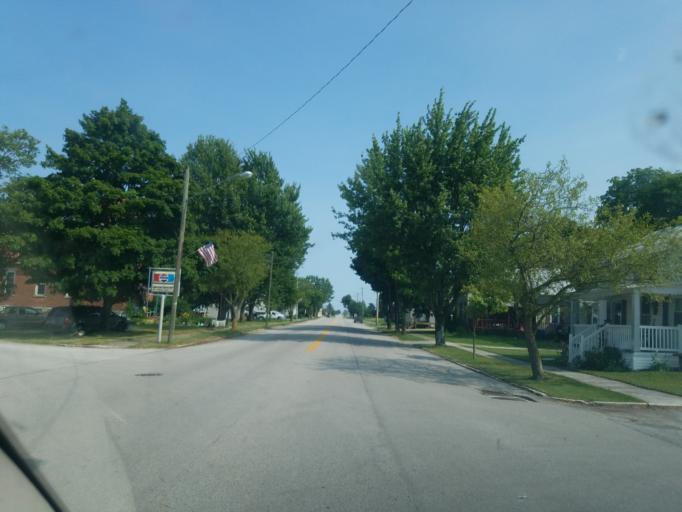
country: US
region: Ohio
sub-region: Wyandot County
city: Carey
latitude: 41.0508
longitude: -83.3177
